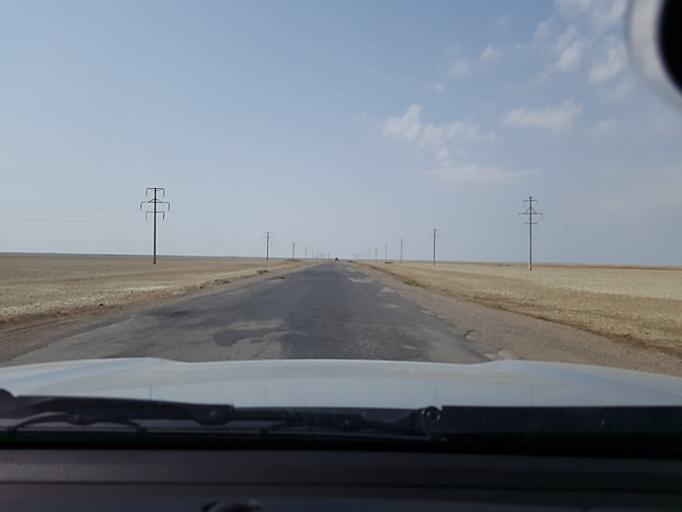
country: TM
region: Balkan
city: Gumdag
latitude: 39.0698
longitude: 54.5843
